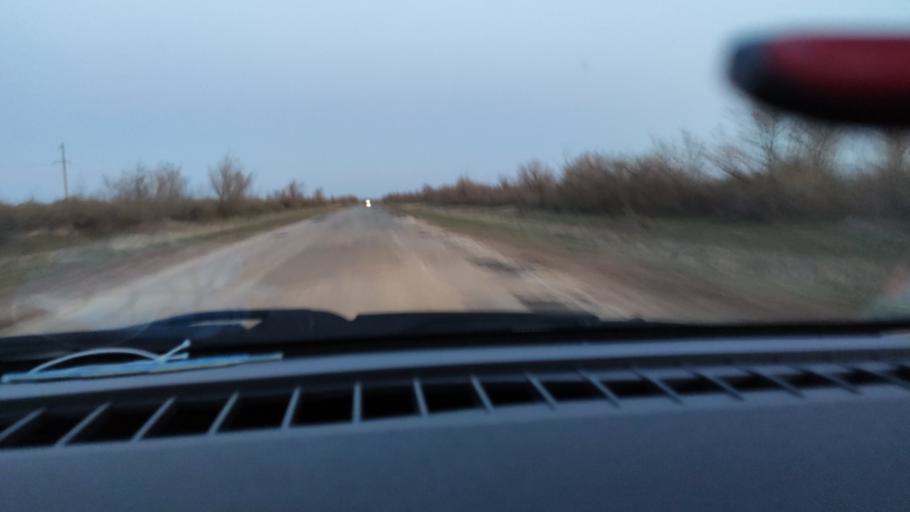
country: RU
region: Saratov
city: Rovnoye
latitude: 51.0517
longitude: 46.0405
